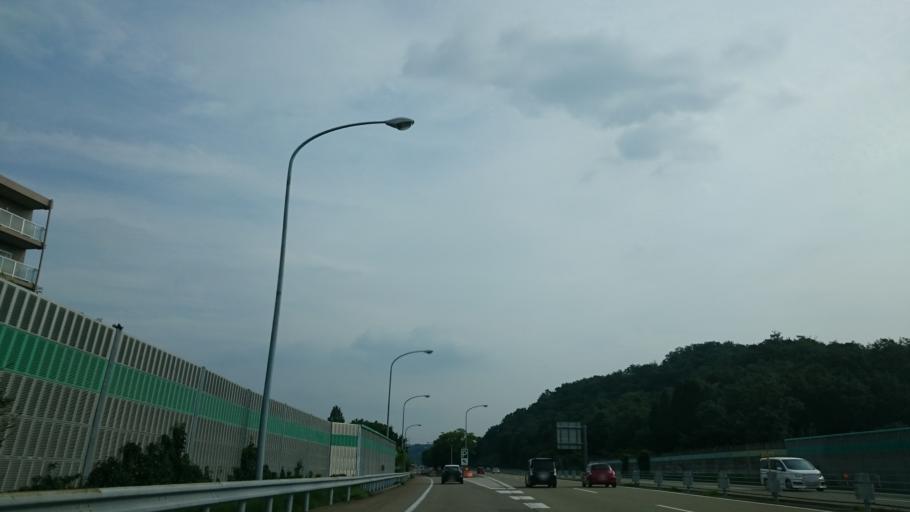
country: JP
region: Gifu
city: Mino
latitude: 35.4930
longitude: 136.8958
